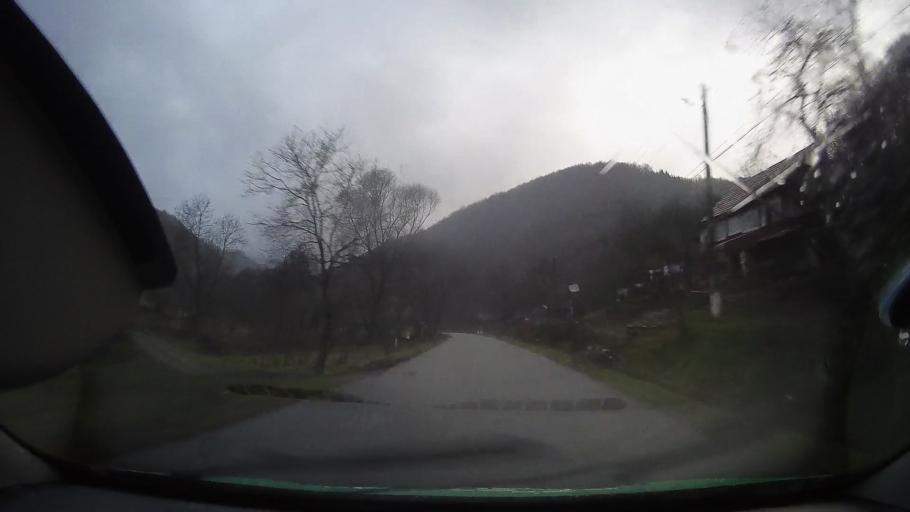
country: RO
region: Hunedoara
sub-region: Comuna Ribita
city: Ribita
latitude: 46.2756
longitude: 22.7414
